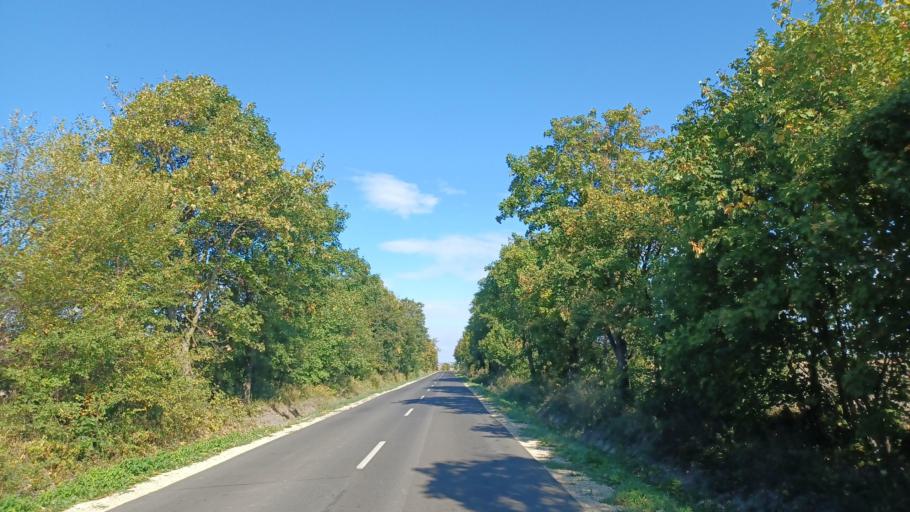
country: HU
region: Tolna
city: Dunaszentgyorgy
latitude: 46.5016
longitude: 18.8260
